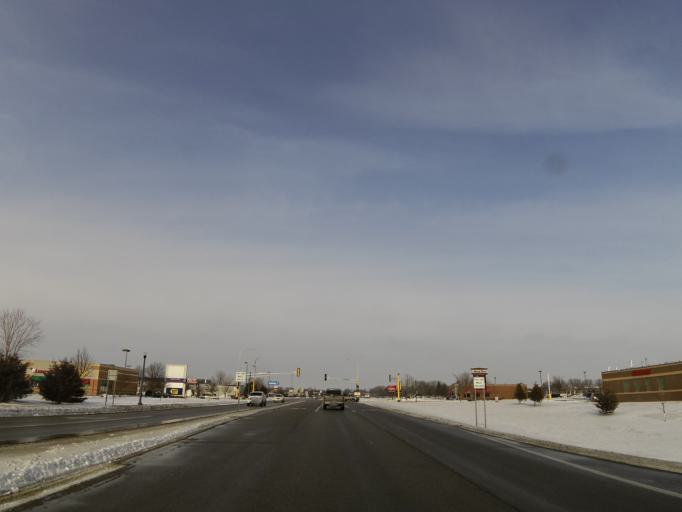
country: US
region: Minnesota
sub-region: McLeod County
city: Hutchinson
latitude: 44.8695
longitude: -94.3755
